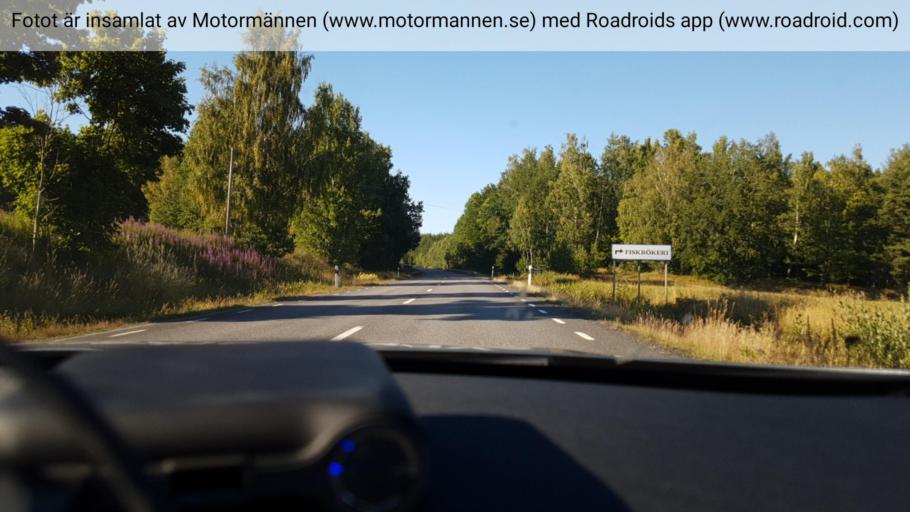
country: SE
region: Joenkoeping
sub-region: Habo Kommun
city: Habo
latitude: 57.9539
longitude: 14.1054
